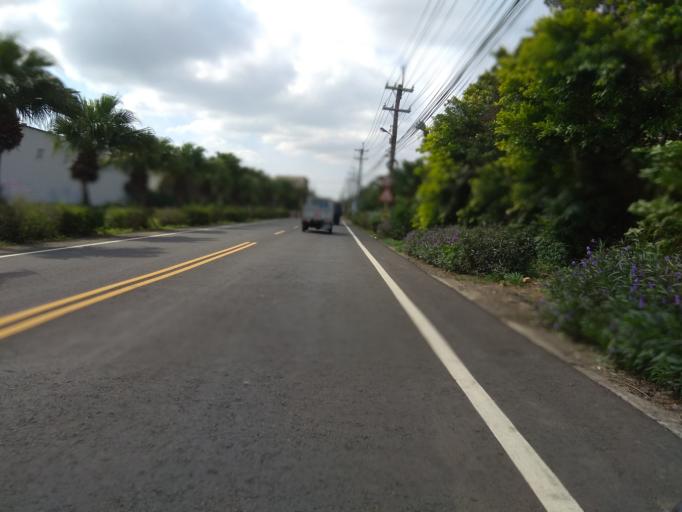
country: TW
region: Taiwan
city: Taoyuan City
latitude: 25.0639
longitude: 121.2383
